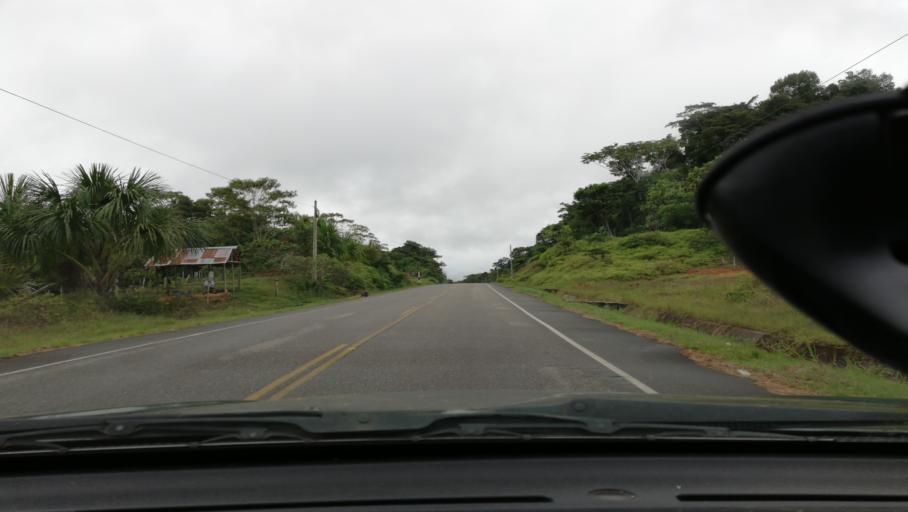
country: PE
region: Loreto
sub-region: Provincia de Loreto
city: Nauta
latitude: -4.3934
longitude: -73.5722
